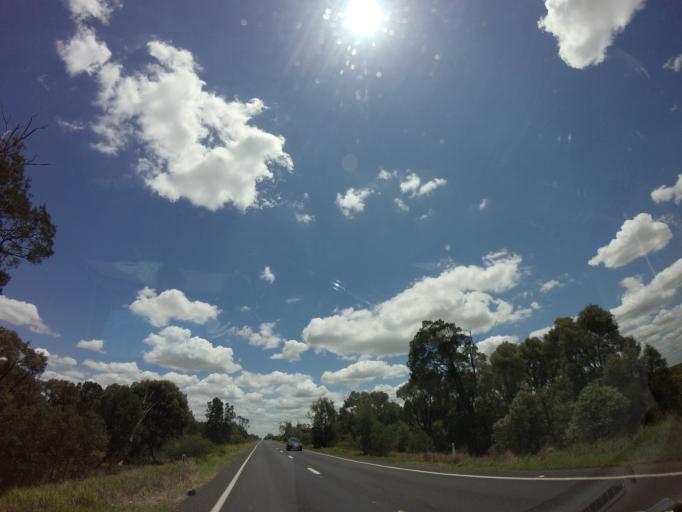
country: AU
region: New South Wales
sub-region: Moree Plains
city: Boggabilla
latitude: -28.7629
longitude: 150.2661
